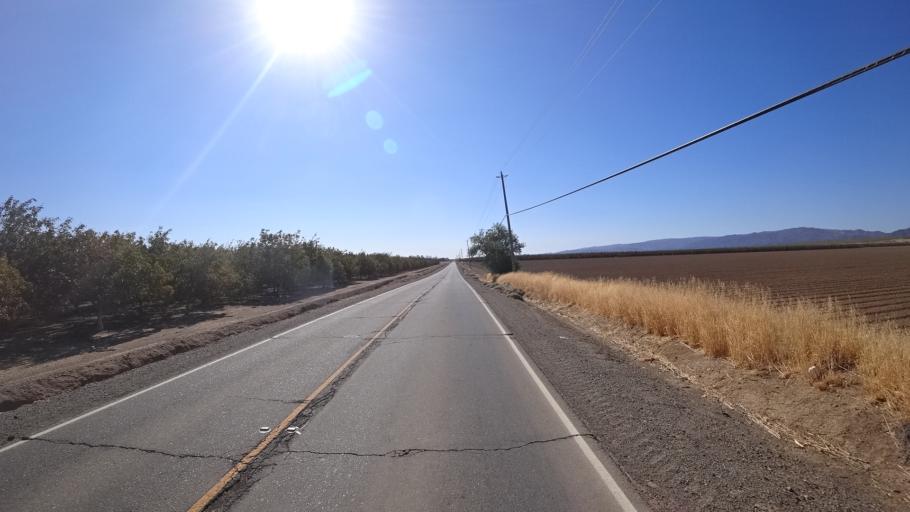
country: US
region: California
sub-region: Yolo County
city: Winters
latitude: 38.5666
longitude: -121.9714
